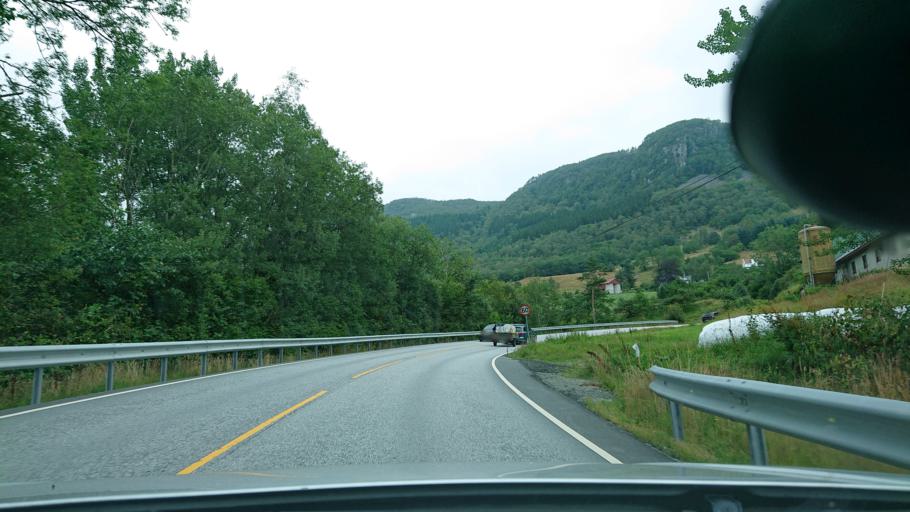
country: NO
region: Rogaland
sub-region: Hjelmeland
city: Hjelmelandsvagen
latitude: 59.1666
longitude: 6.1675
